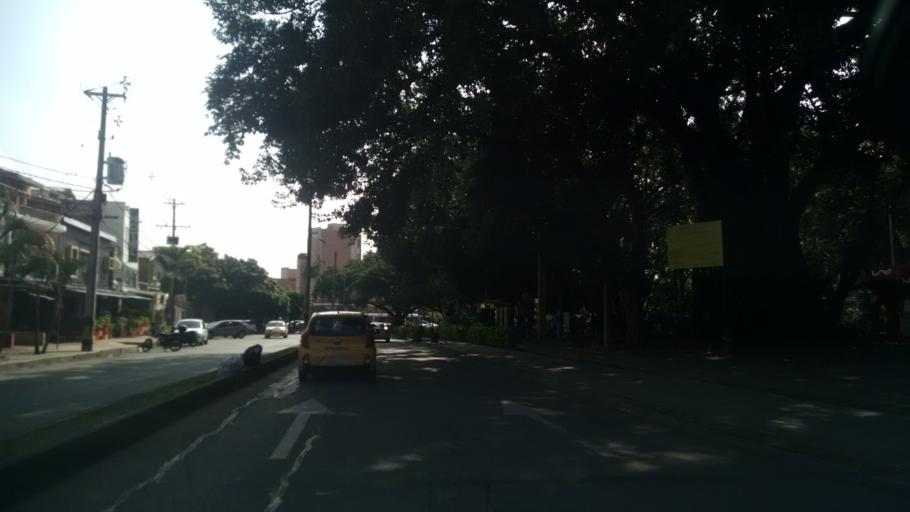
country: CO
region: Antioquia
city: Medellin
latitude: 6.2463
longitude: -75.5938
